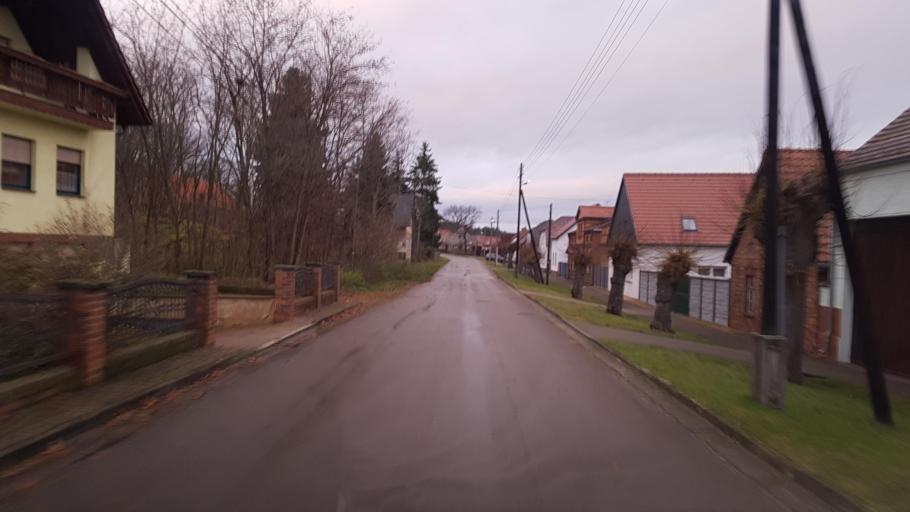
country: DE
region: Brandenburg
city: Luebben
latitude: 51.9059
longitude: 13.8089
